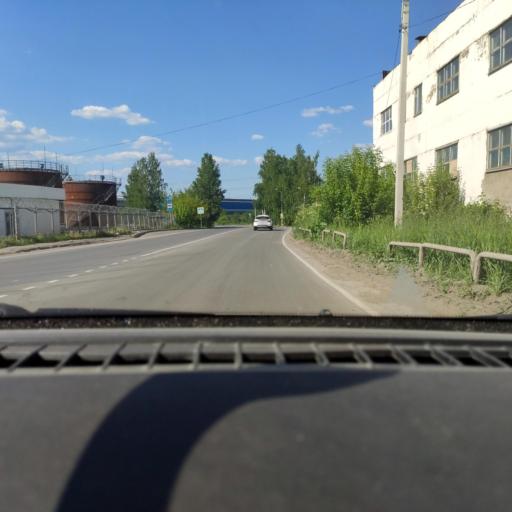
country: RU
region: Perm
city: Krasnokamsk
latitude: 58.0726
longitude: 55.7831
